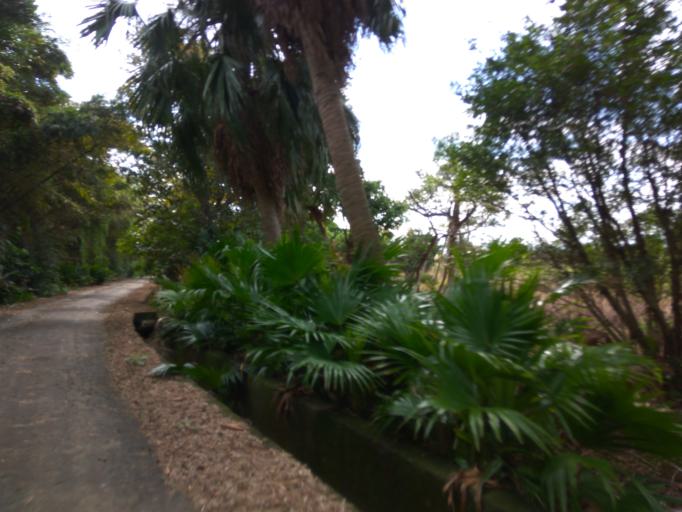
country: TW
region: Taiwan
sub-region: Hsinchu
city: Zhubei
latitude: 24.9563
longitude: 121.1070
